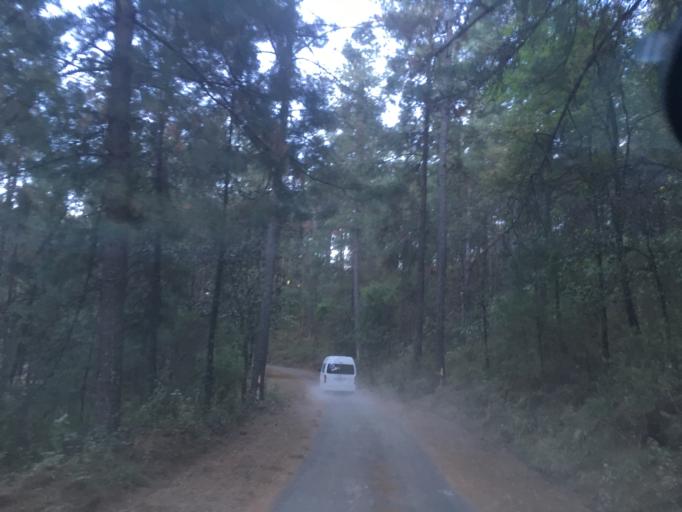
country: MX
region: Michoacan
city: Angahuan
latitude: 19.4918
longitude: -102.2068
